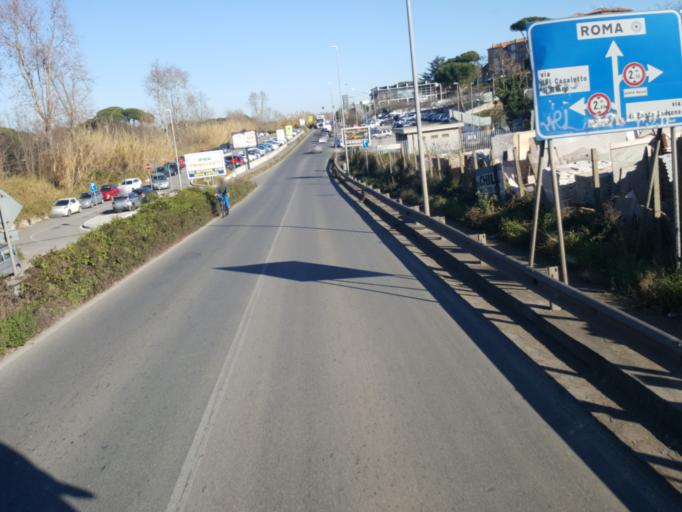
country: IT
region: Latium
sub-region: Citta metropolitana di Roma Capitale
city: Vitinia
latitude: 41.7884
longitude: 12.3743
